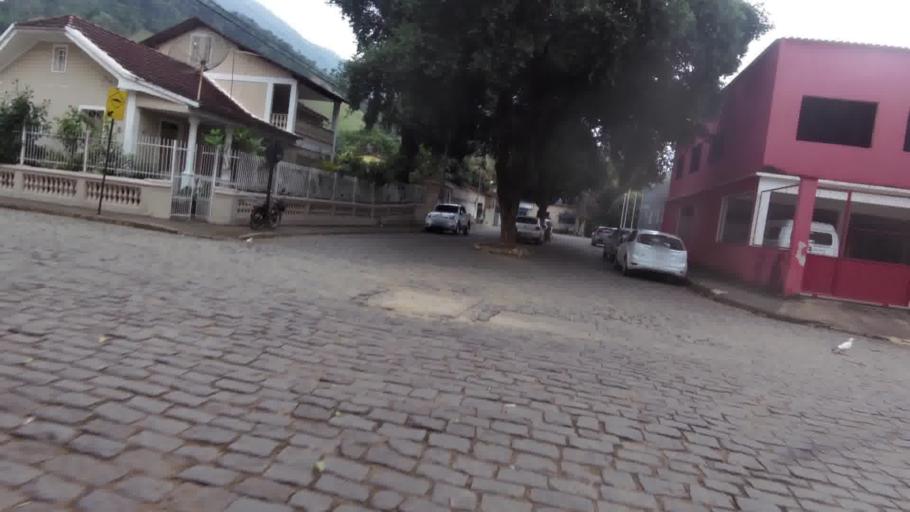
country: BR
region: Espirito Santo
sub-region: Alfredo Chaves
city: Alfredo Chaves
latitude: -20.6353
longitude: -40.7486
